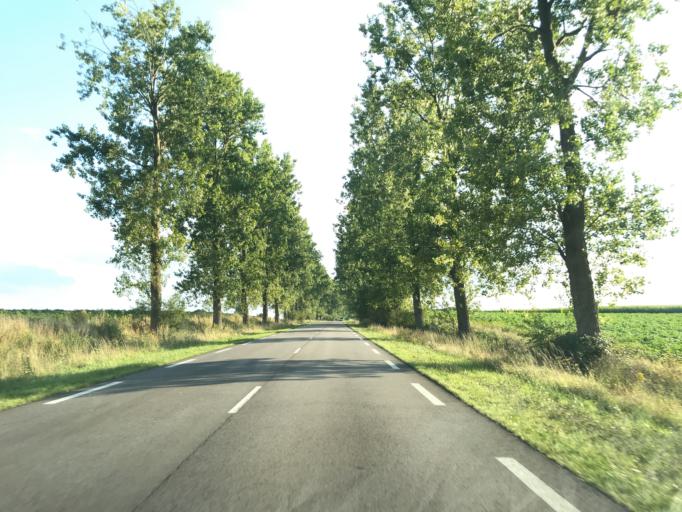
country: FR
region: Haute-Normandie
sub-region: Departement de la Seine-Maritime
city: Saint-Eustache-la-Foret
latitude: 49.5463
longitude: 0.4332
